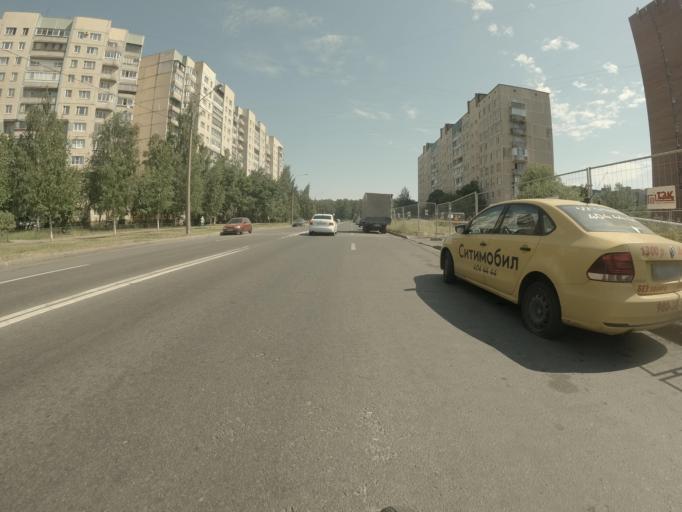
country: RU
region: St.-Petersburg
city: Krasnogvargeisky
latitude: 59.9561
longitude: 30.4903
